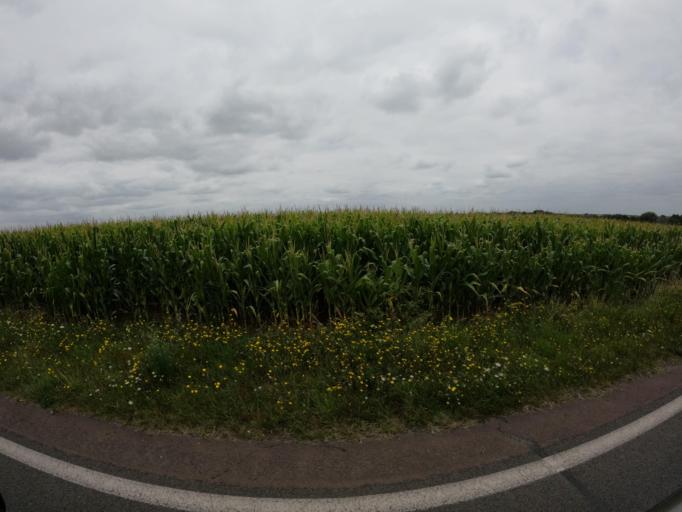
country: FR
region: Pays de la Loire
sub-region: Departement de la Vendee
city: Maillezais
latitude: 46.4166
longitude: -0.6998
